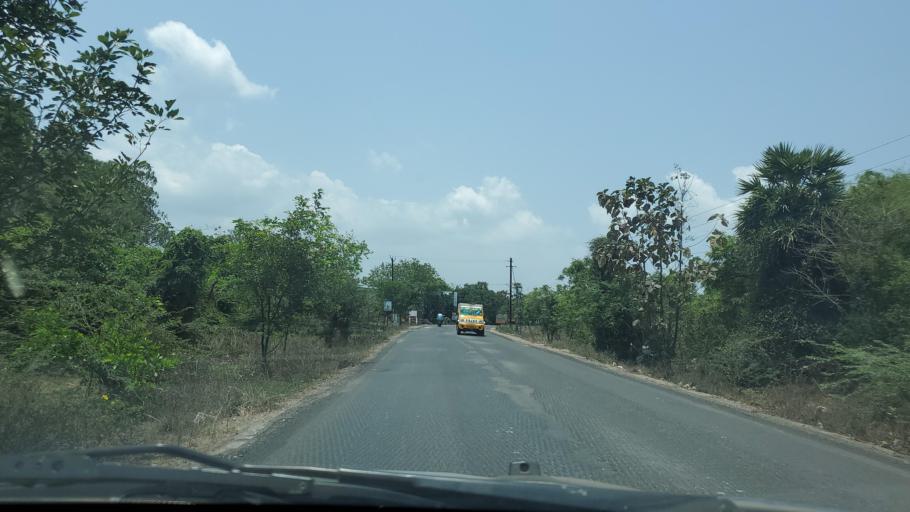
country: IN
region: Tamil Nadu
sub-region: Kancheepuram
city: Vengavasal
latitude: 12.8751
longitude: 80.1713
